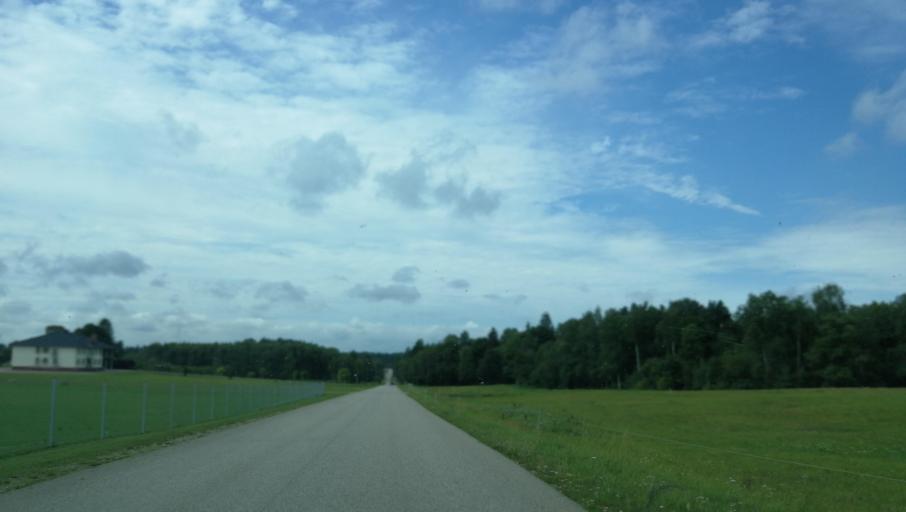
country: LV
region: Cesu Rajons
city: Cesis
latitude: 57.3275
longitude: 25.2862
